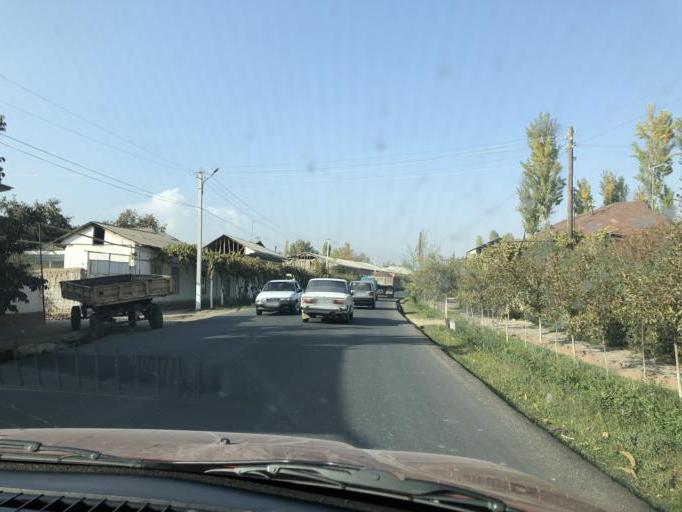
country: UZ
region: Namangan
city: Chust Shahri
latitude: 41.0674
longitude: 71.2050
